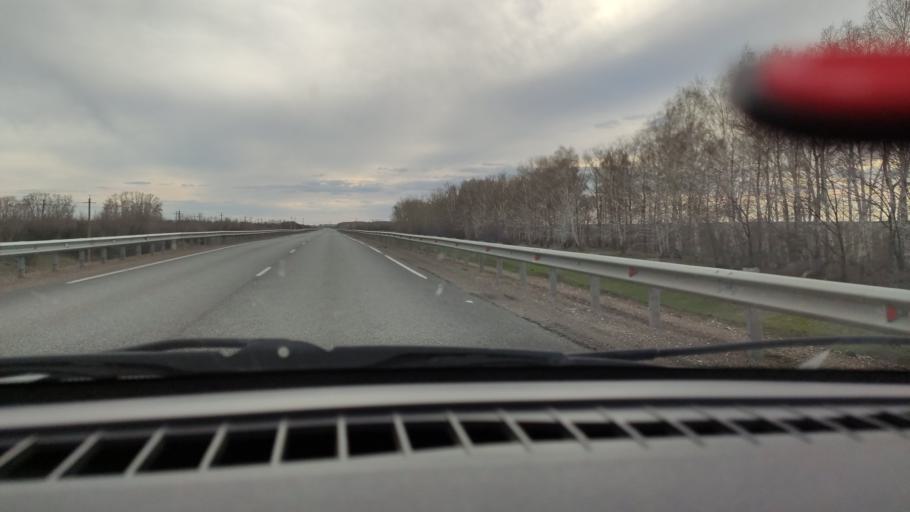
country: RU
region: Bashkortostan
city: Mayachnyy
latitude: 52.4040
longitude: 55.7222
